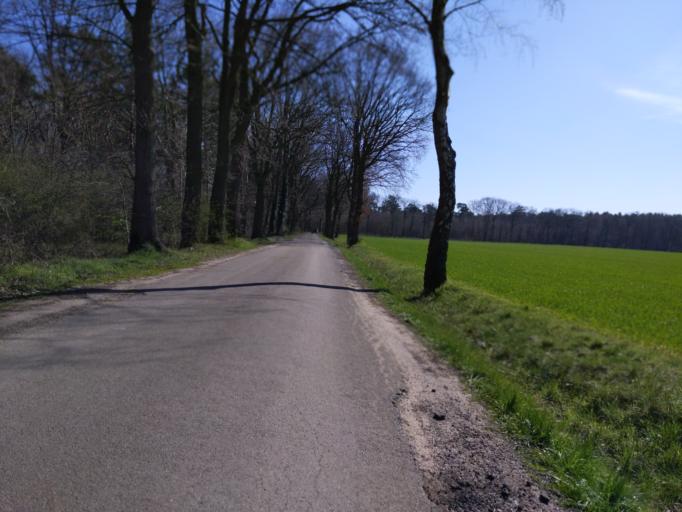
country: DE
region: North Rhine-Westphalia
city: Dorsten
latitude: 51.6951
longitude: 6.9758
